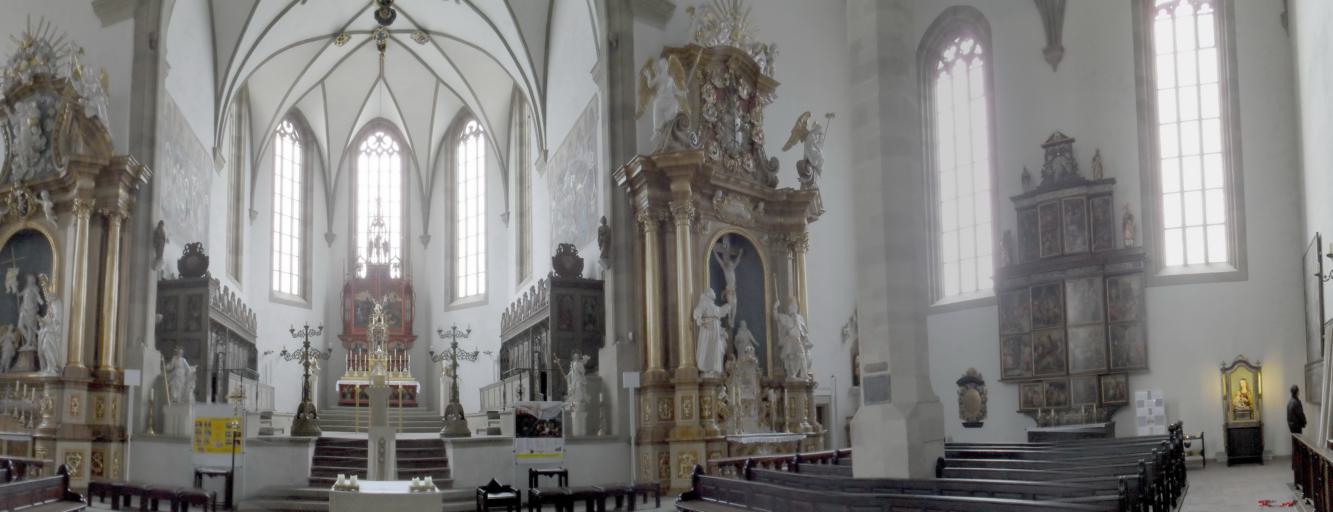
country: DE
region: Bavaria
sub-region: Regierungsbezirk Unterfranken
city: Wuerzburg
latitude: 49.7899
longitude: 9.9249
